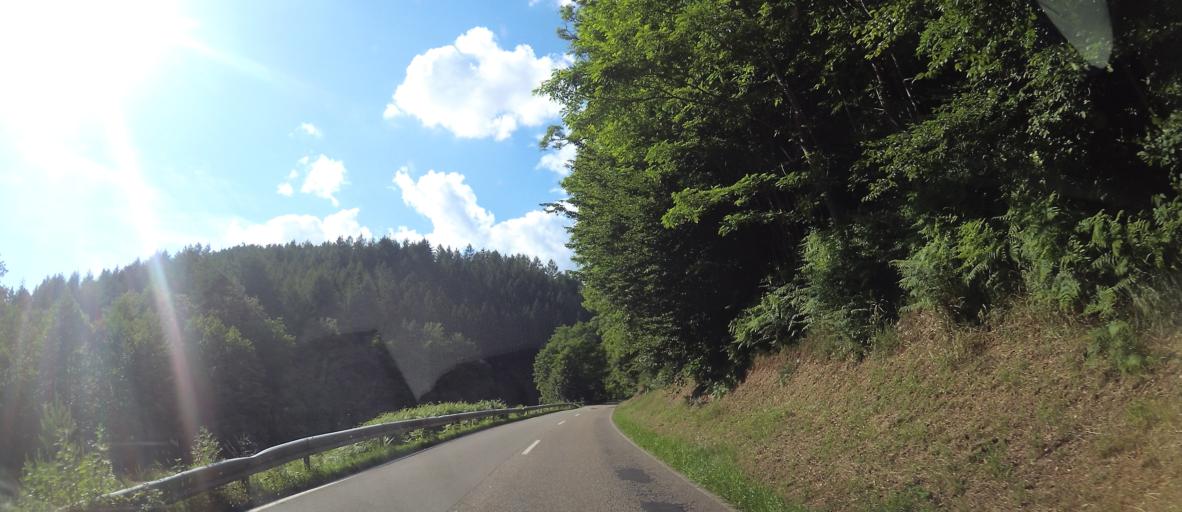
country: DE
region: Rheinland-Pfalz
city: Trulben
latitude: 49.1201
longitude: 7.5453
